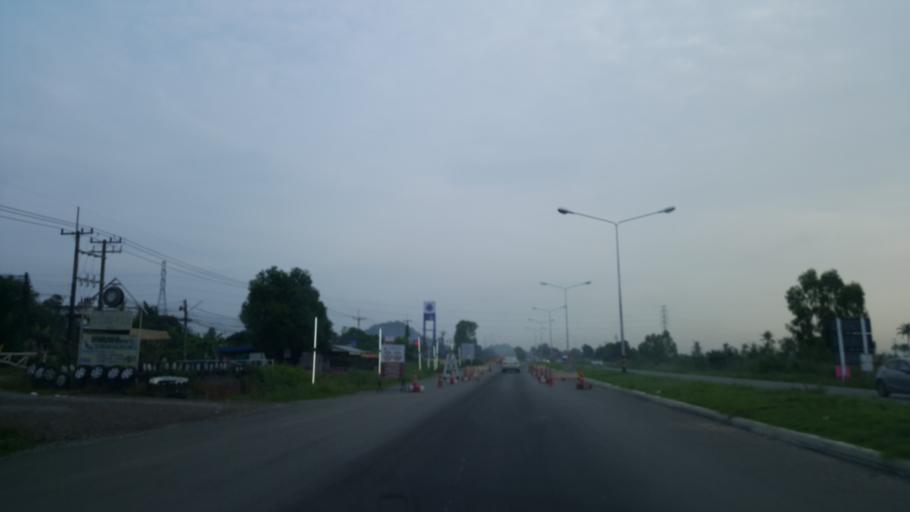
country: TH
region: Rayong
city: Ban Chang
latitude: 12.7271
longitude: 100.9826
